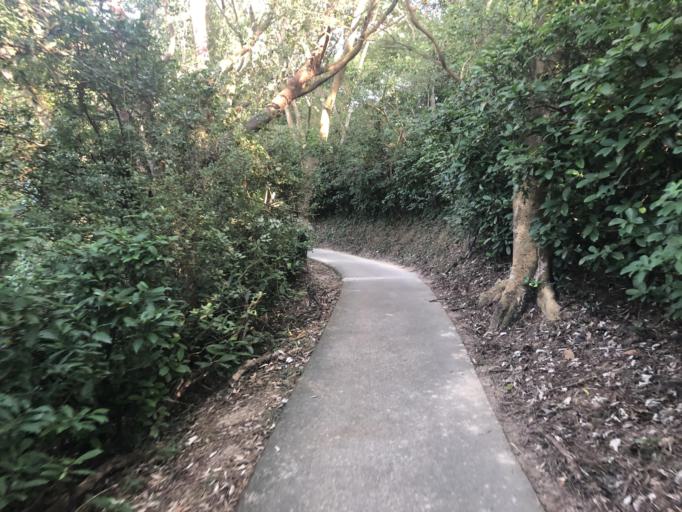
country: HK
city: Yung Shue Wan
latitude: 22.2151
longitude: 114.0275
